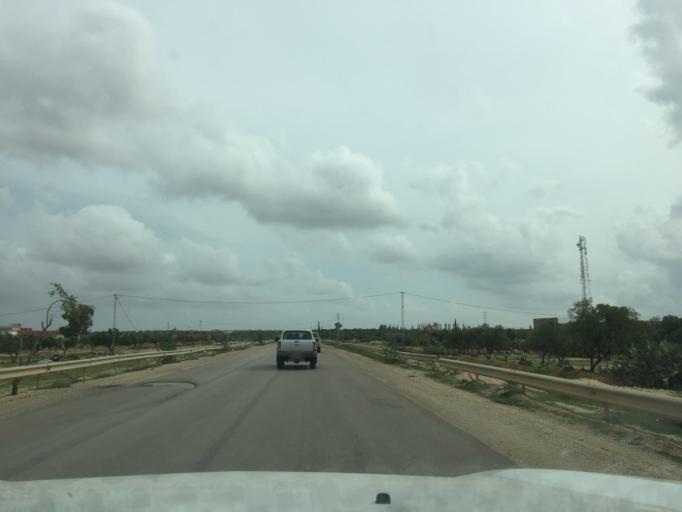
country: TN
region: Al Munastir
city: Jammal
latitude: 35.6053
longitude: 10.7581
